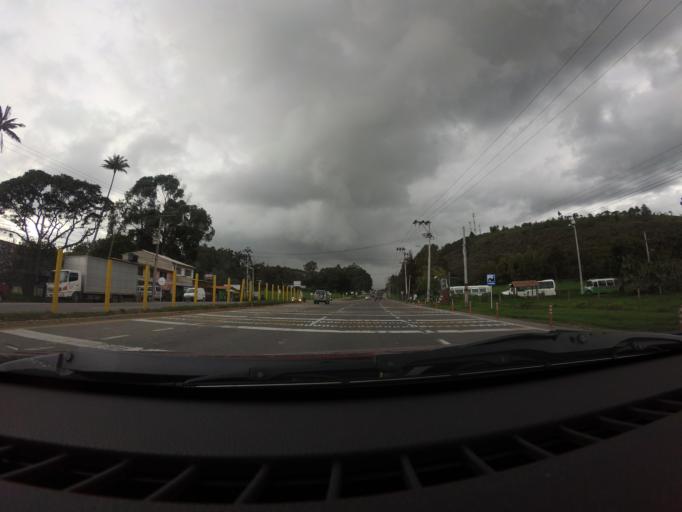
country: CO
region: Cundinamarca
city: El Rosal
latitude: 4.7998
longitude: -74.2093
